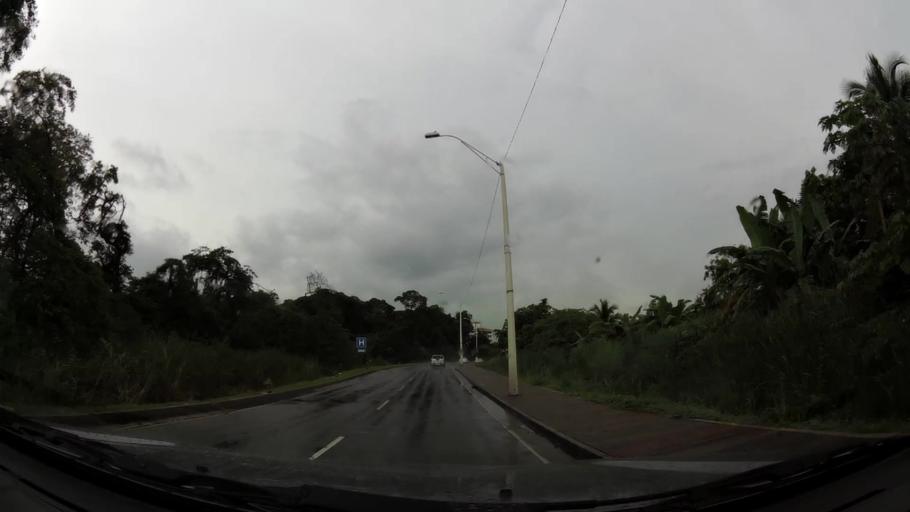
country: PA
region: Colon
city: Arco Iris
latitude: 9.3411
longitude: -79.8895
